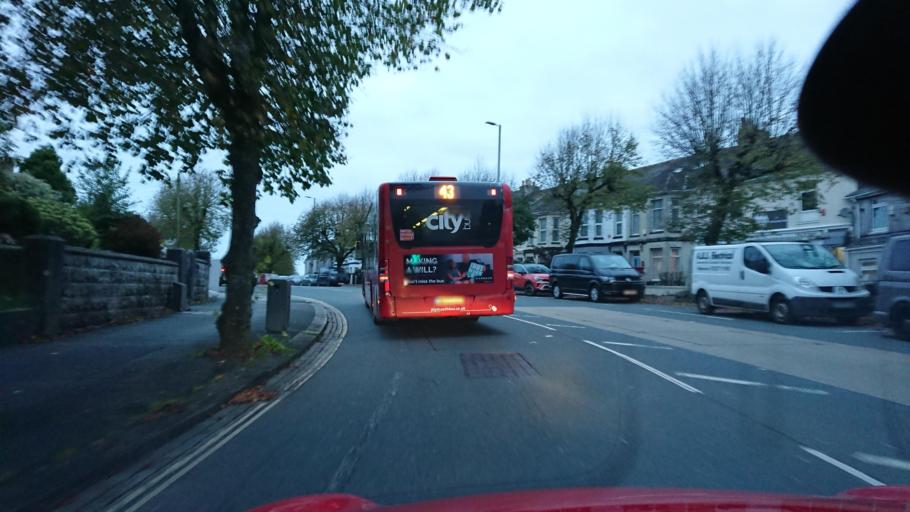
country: GB
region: England
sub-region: Cornwall
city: Torpoint
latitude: 50.4102
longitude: -4.1803
